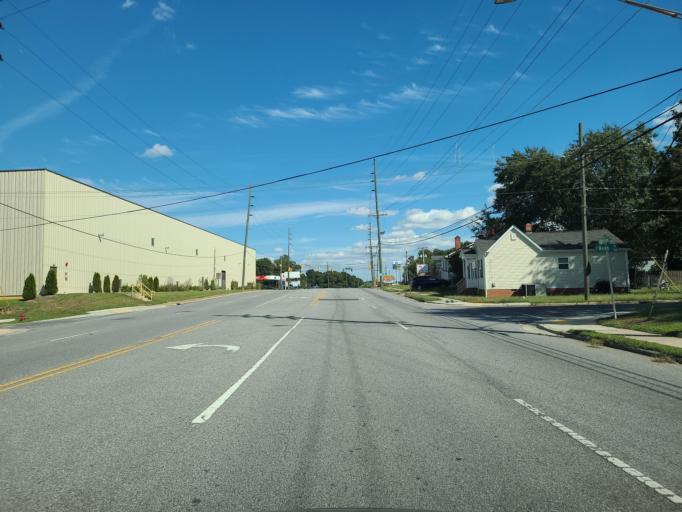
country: US
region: North Carolina
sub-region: Gaston County
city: Gastonia
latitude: 35.2577
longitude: -81.2091
